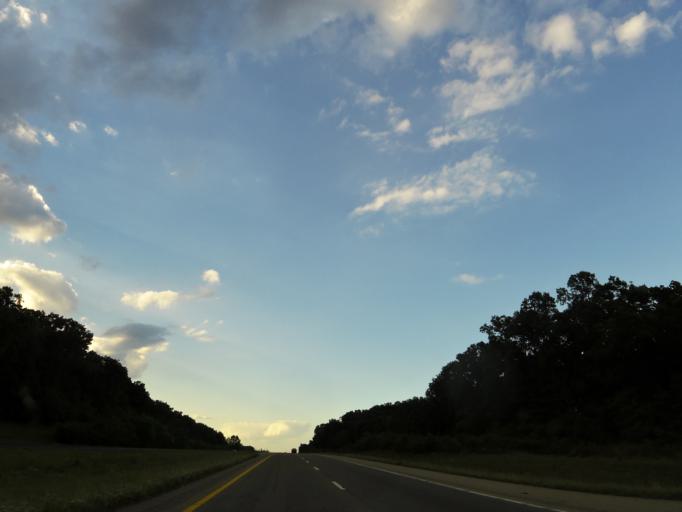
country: US
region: Tennessee
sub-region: Maury County
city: Spring Hill
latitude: 35.7102
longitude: -86.8801
